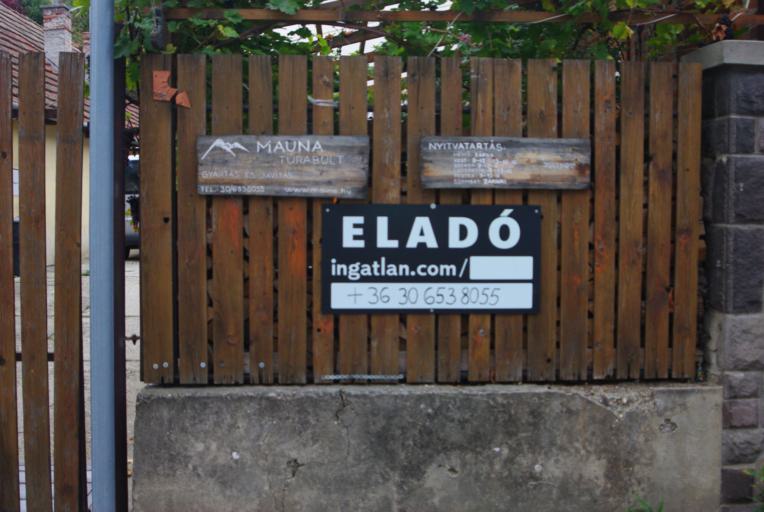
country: HU
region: Pest
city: Nagymaros
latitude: 47.7965
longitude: 18.9593
